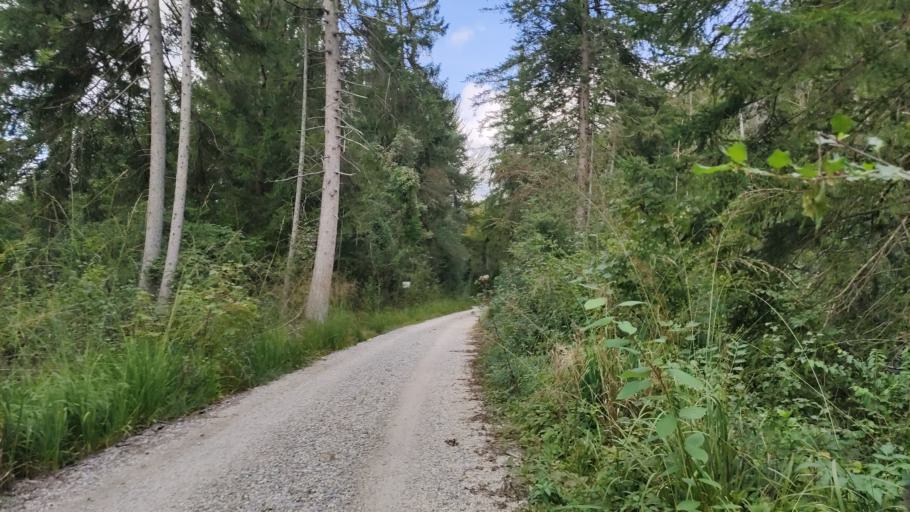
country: DE
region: Bavaria
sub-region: Upper Bavaria
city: Kaufering
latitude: 48.1274
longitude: 10.8599
